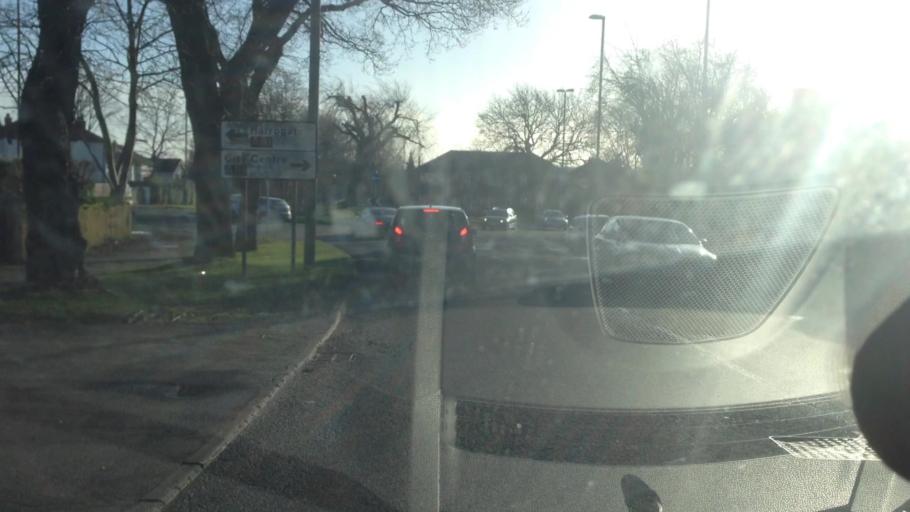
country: GB
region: England
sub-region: City and Borough of Leeds
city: Chapel Allerton
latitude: 53.8401
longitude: -1.5437
